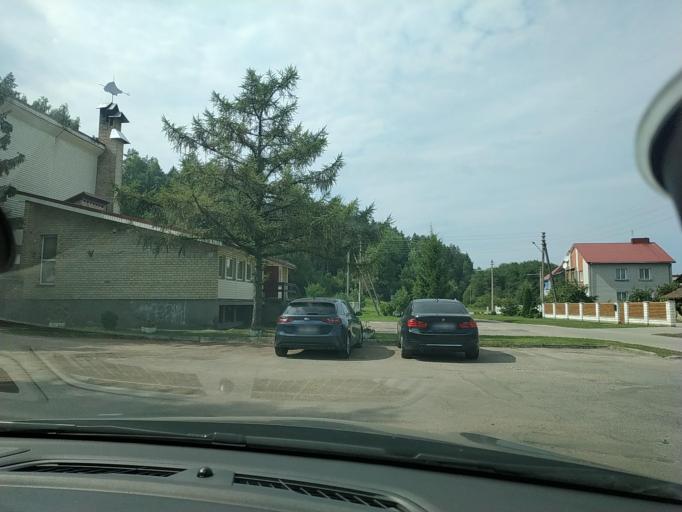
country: LT
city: Nemencine
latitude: 54.8393
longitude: 25.4628
